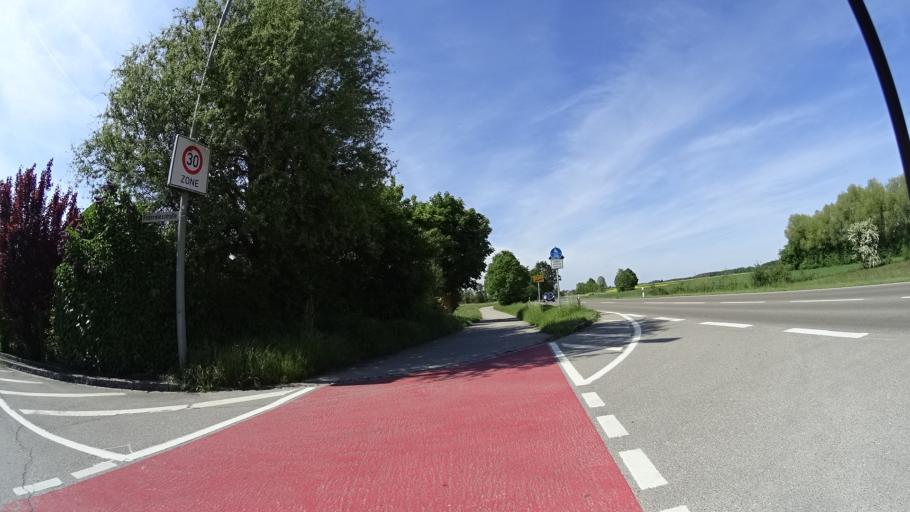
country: DE
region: Bavaria
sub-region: Swabia
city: Pfaffenhofen an der Roth
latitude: 48.3308
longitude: 10.1613
